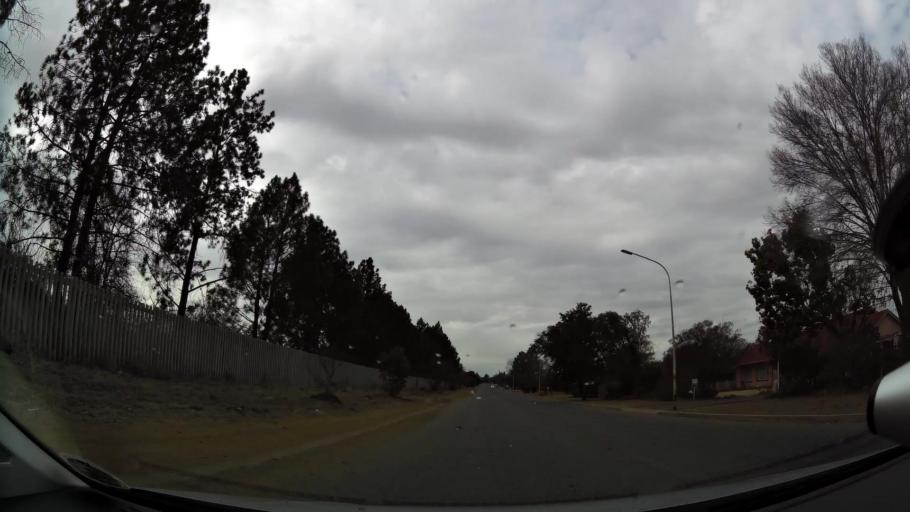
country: ZA
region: Orange Free State
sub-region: Fezile Dabi District Municipality
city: Kroonstad
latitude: -27.6318
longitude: 27.2183
